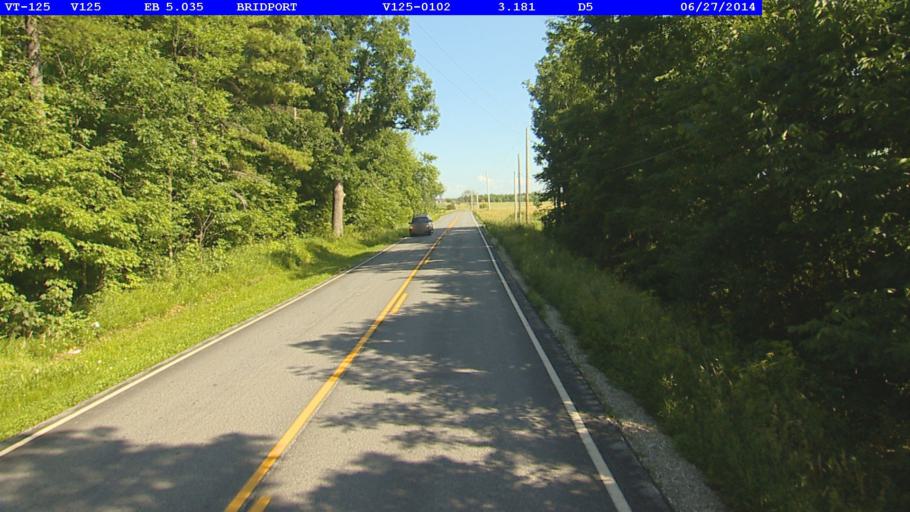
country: US
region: New York
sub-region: Essex County
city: Port Henry
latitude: 43.9942
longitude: -73.3497
